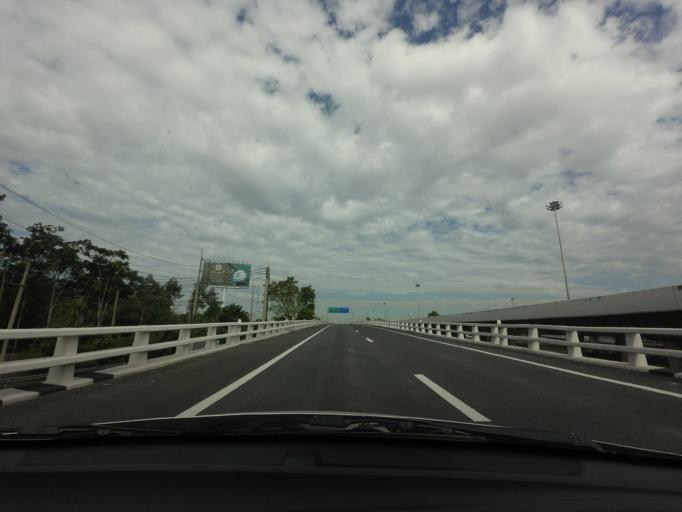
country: TH
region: Pathum Thani
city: Thanyaburi
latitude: 14.0056
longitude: 100.7056
